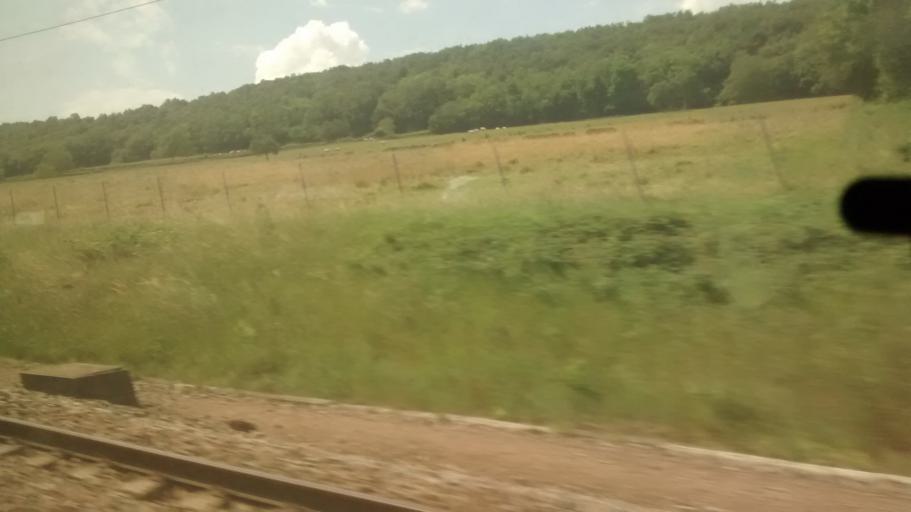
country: FR
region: Bourgogne
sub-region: Departement de Saone-et-Loire
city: Saint-Gengoux-le-National
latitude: 46.6398
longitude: 4.5865
